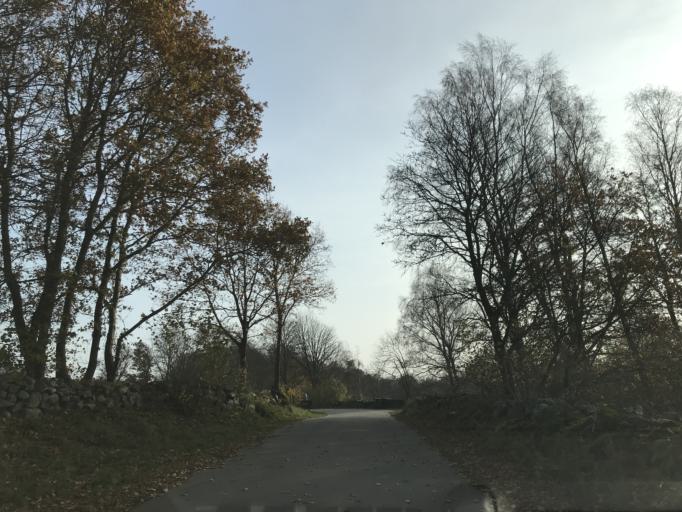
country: SE
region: Skane
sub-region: Klippans Kommun
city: Ljungbyhed
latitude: 56.0682
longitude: 13.2845
